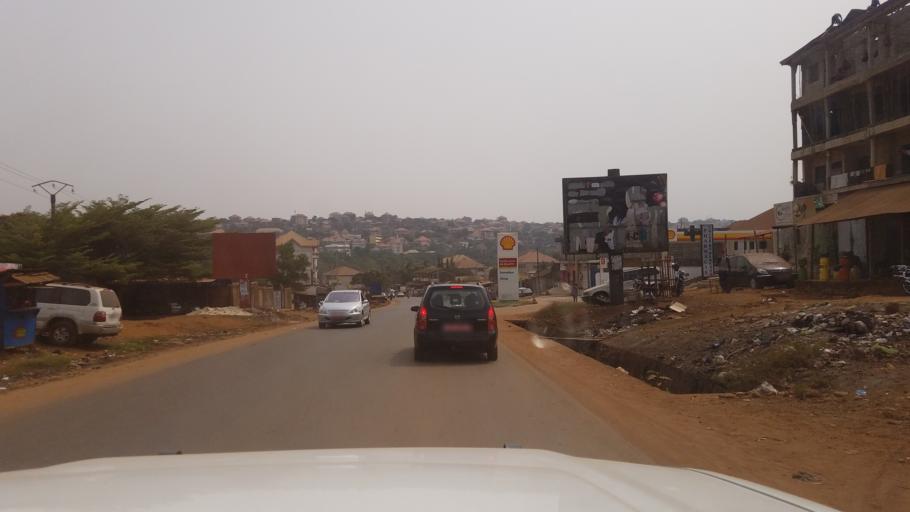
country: GN
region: Conakry
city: Conakry
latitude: 9.6461
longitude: -13.6064
